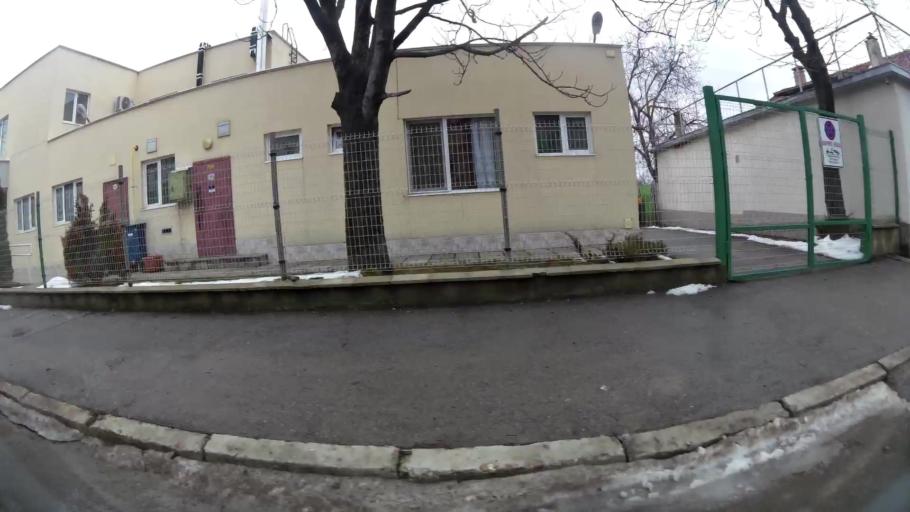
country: BG
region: Sofiya
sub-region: Obshtina Bozhurishte
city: Bozhurishte
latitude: 42.6733
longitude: 23.2384
